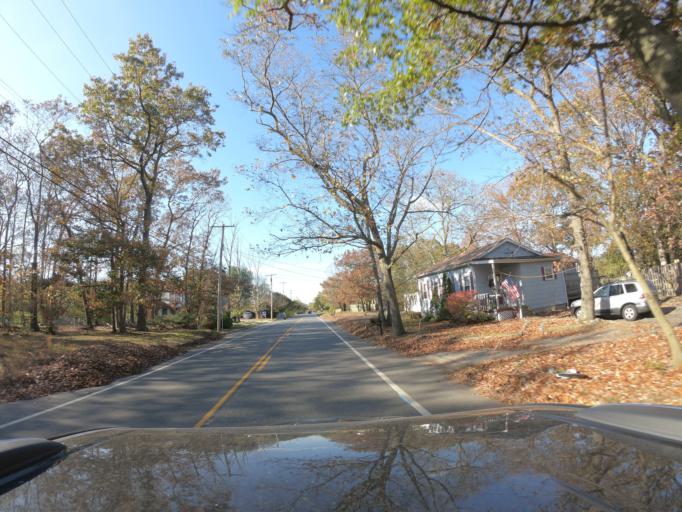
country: US
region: New Jersey
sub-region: Monmouth County
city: Ramtown
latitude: 40.0937
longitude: -74.1580
